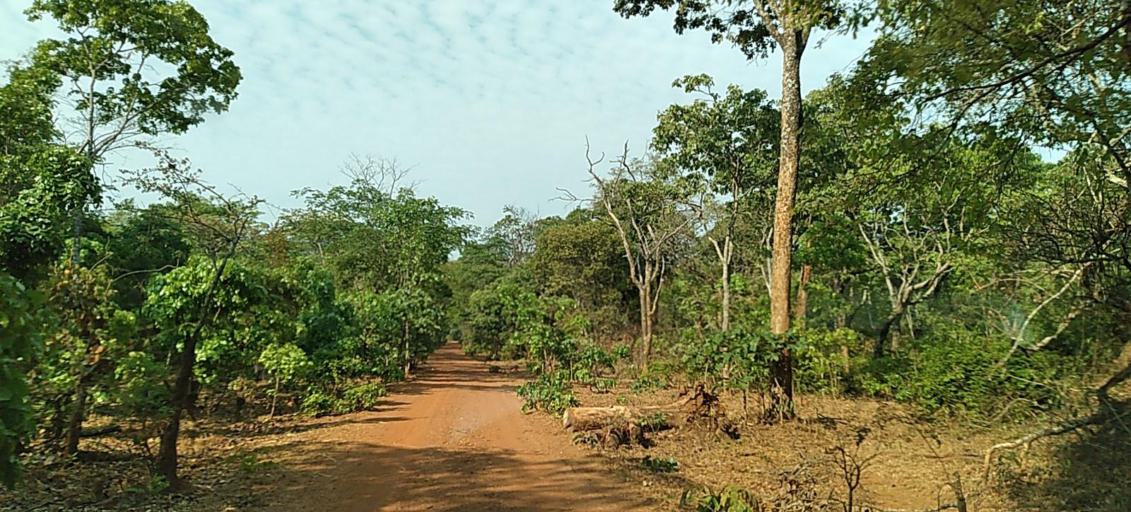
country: ZM
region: Copperbelt
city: Kalulushi
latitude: -12.9958
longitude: 27.7118
